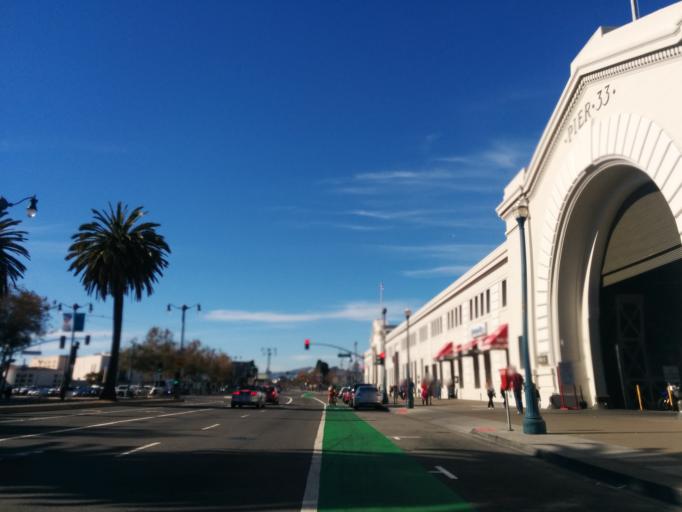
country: US
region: California
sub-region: San Francisco County
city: San Francisco
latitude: 37.8065
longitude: -122.4050
